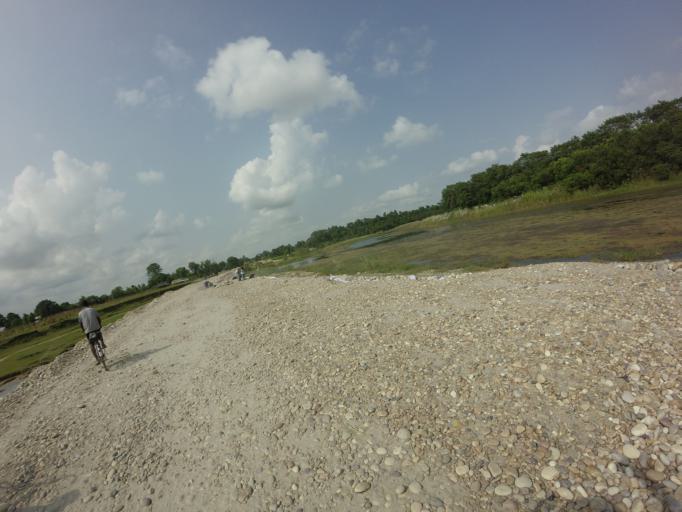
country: NP
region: Far Western
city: Tikapur
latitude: 28.4499
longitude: 81.0734
